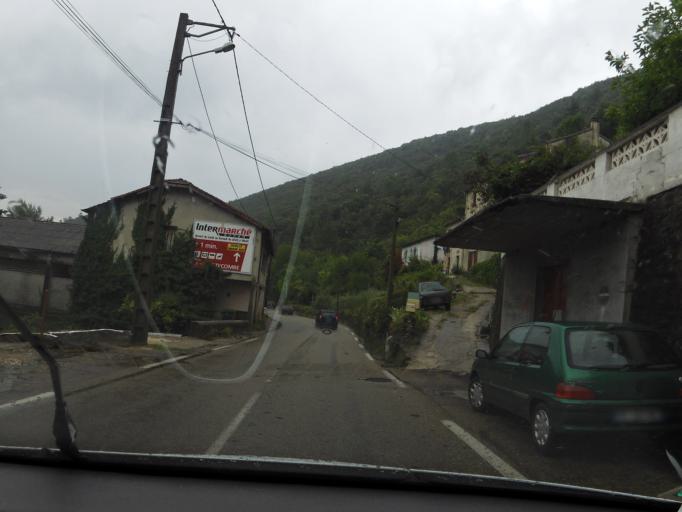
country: FR
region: Languedoc-Roussillon
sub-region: Departement du Gard
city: Les Salles-du-Gardon
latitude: 44.2085
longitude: 4.0228
